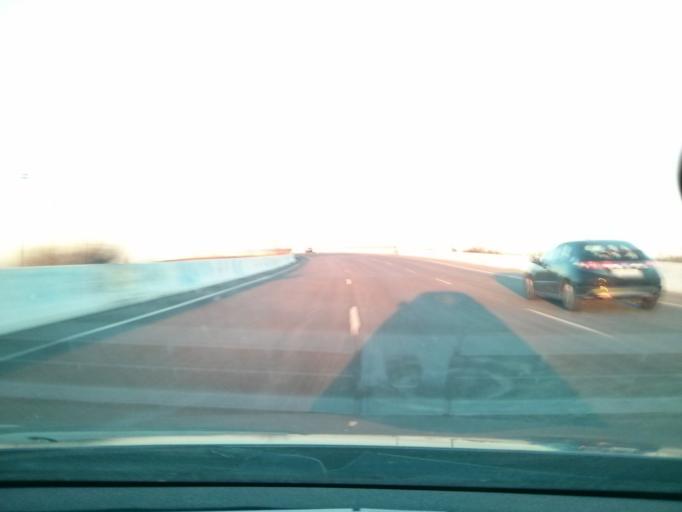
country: ES
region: Madrid
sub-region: Provincia de Madrid
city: Las Tablas
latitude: 40.5101
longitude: -3.6555
